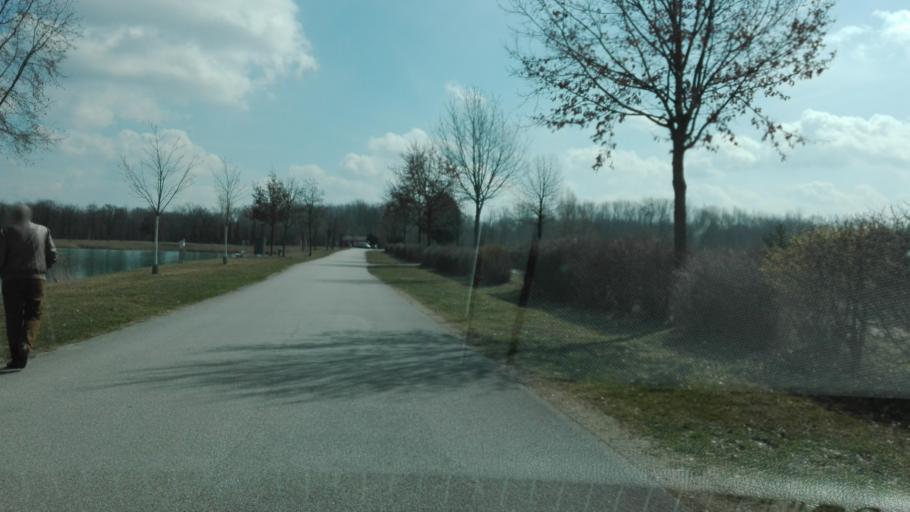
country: AT
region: Upper Austria
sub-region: Politischer Bezirk Urfahr-Umgebung
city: Feldkirchen an der Donau
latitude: 48.3257
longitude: 14.0714
